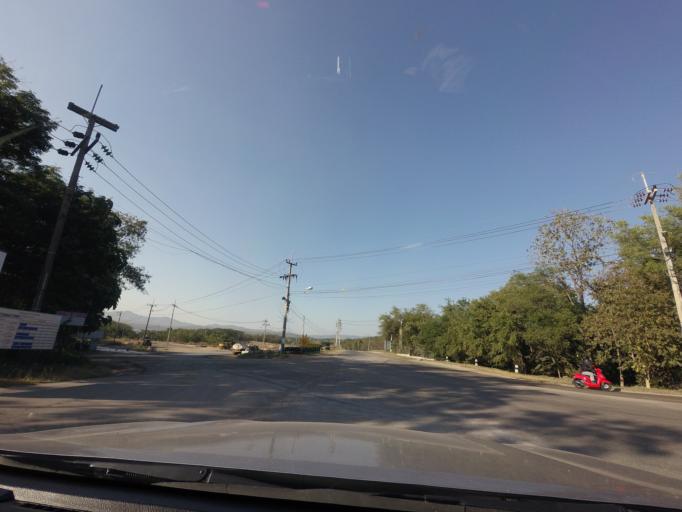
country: TH
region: Lampang
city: Mae Mo
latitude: 18.3277
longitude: 99.7460
